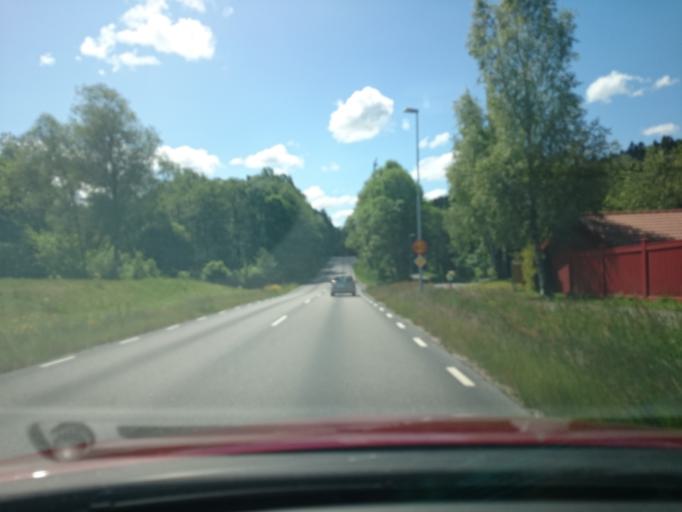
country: SE
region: Vaestra Goetaland
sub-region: Harryda Kommun
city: Landvetter
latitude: 57.6942
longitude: 12.2065
